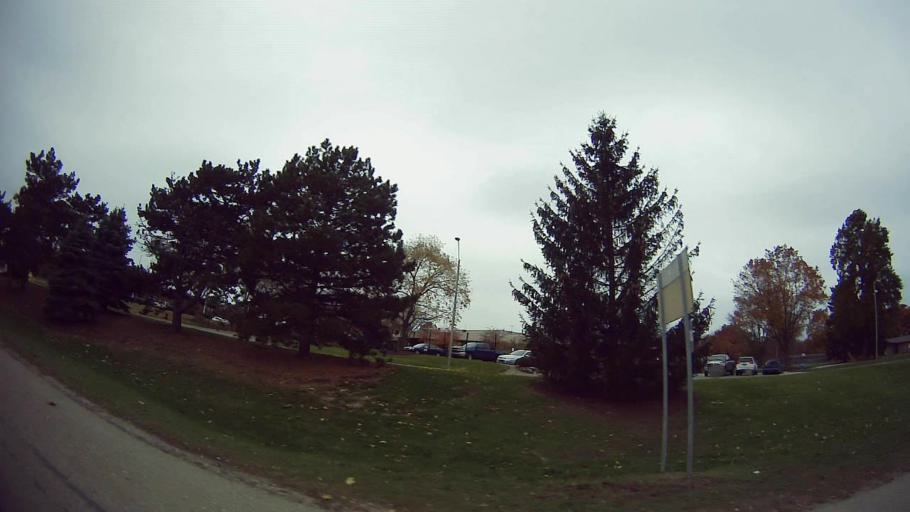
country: US
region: Michigan
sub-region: Oakland County
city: Pontiac
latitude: 42.6599
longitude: -83.3351
